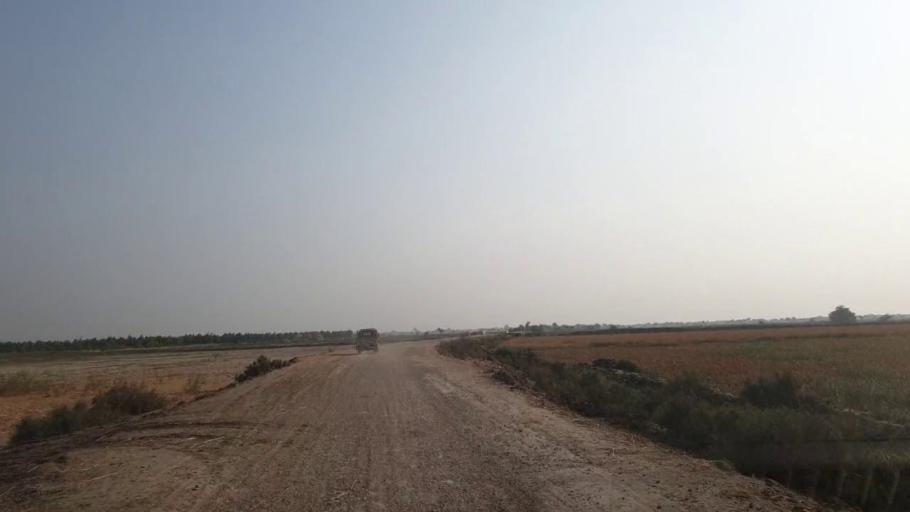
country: PK
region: Sindh
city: Kario
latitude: 24.9131
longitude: 68.5688
